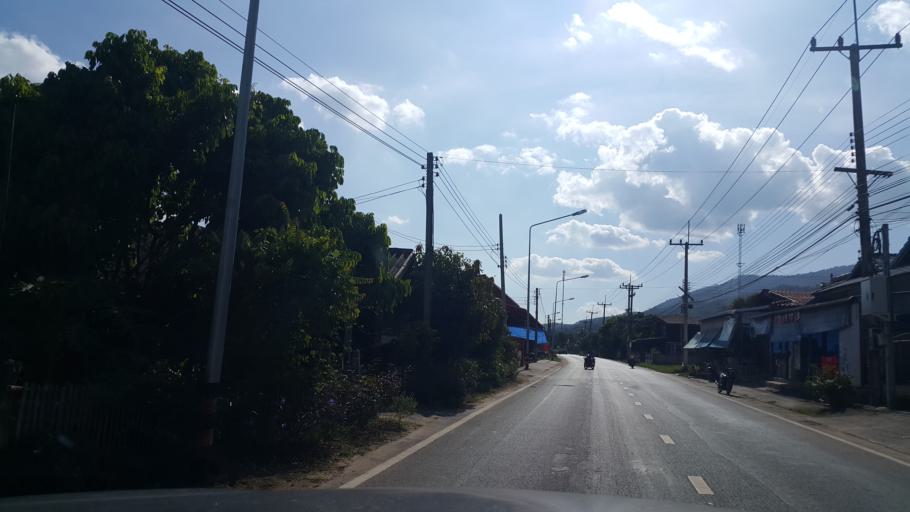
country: TH
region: Lamphun
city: Mae Tha
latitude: 18.5538
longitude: 99.2493
